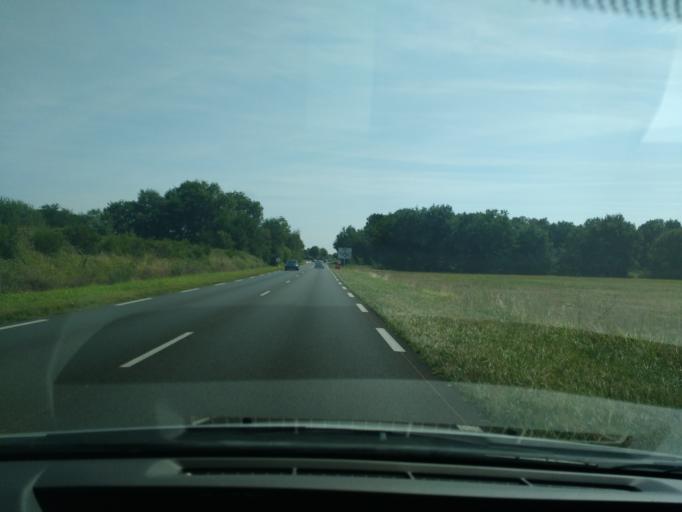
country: FR
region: Pays de la Loire
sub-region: Departement de Maine-et-Loire
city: Andard
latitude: 47.4651
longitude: -0.4135
